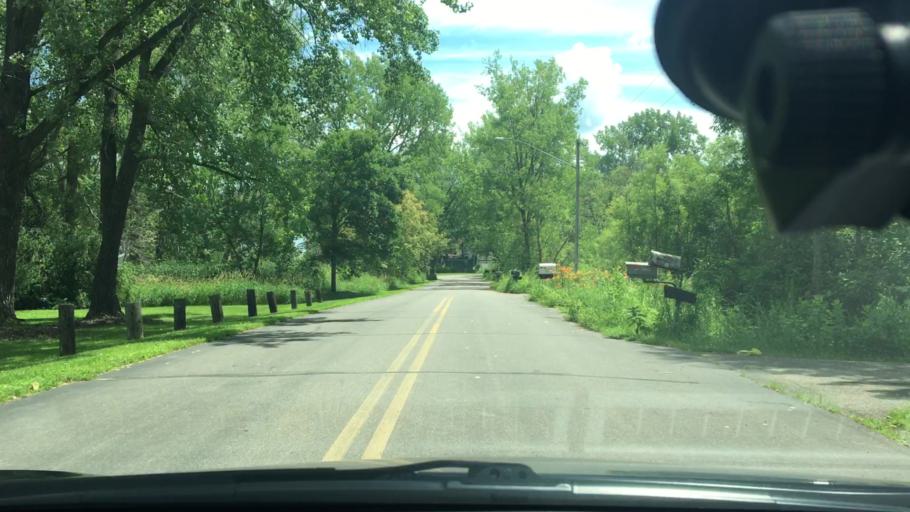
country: US
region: Minnesota
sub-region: Hennepin County
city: Plymouth
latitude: 45.0021
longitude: -93.4232
